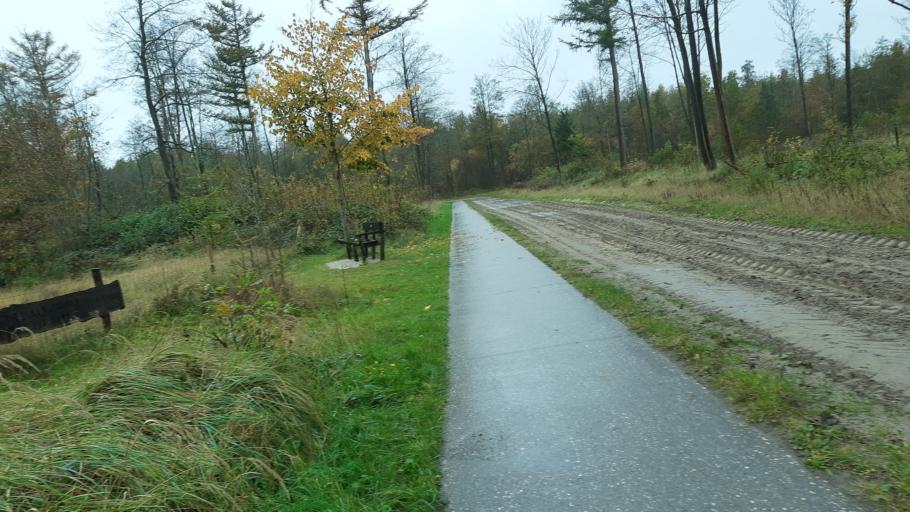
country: NL
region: Friesland
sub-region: Gemeente Lemsterland
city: Echtenerbrug
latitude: 52.7822
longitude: 5.8051
